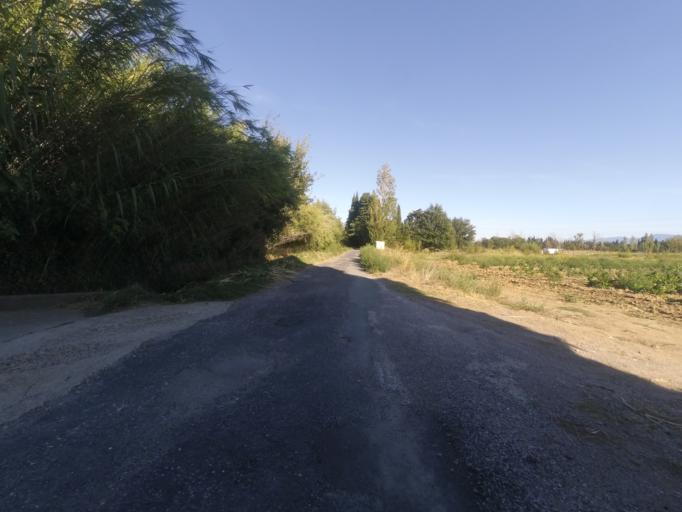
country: FR
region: Languedoc-Roussillon
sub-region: Departement des Pyrenees-Orientales
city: Corneilla-la-Riviere
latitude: 42.6986
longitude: 2.7156
